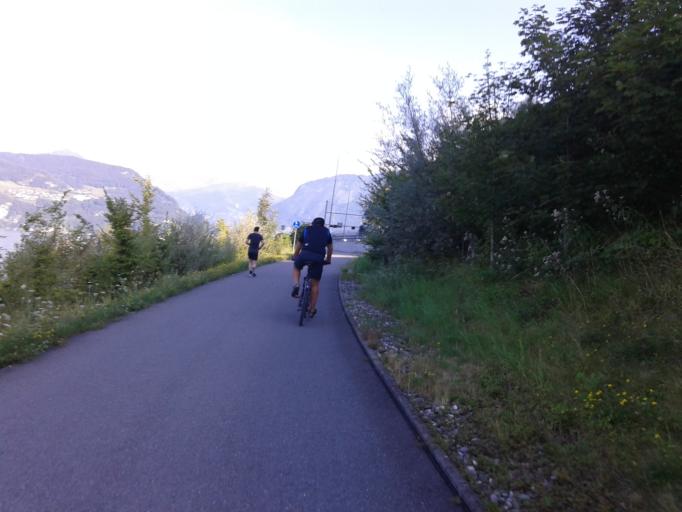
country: CH
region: Lucerne
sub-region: Lucerne-Land District
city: Horw
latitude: 47.0035
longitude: 8.3087
